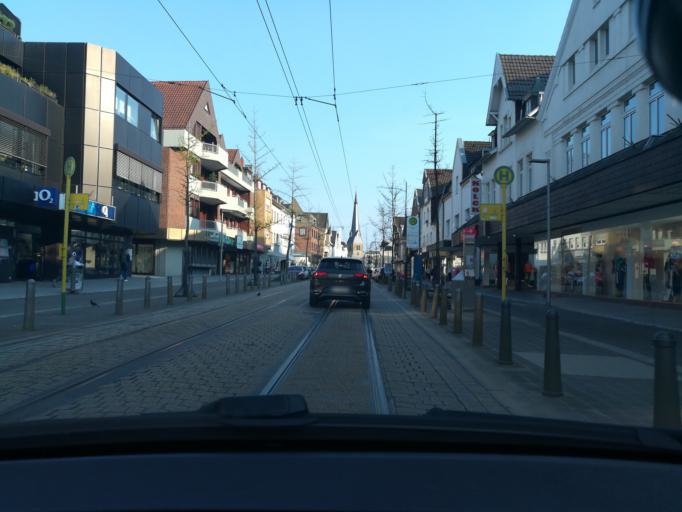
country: DE
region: North Rhine-Westphalia
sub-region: Regierungsbezirk Detmold
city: Bielefeld
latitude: 51.9908
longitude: 8.5107
